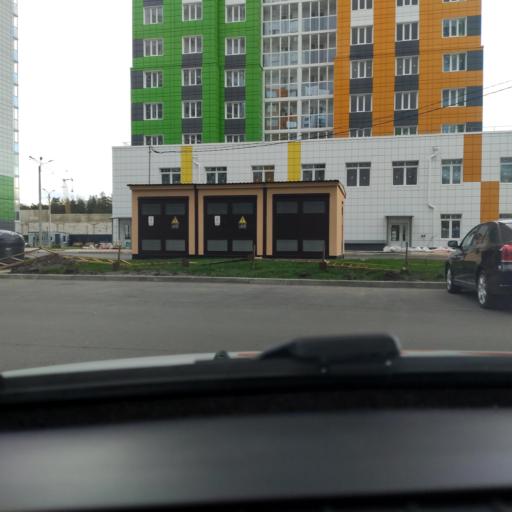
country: RU
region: Voronezj
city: Podgornoye
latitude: 51.7592
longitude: 39.1838
